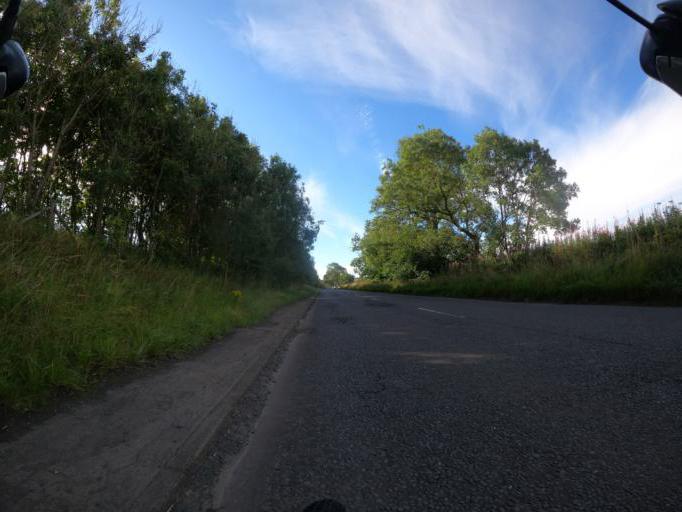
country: GB
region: Scotland
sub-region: Edinburgh
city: Newbridge
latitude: 55.9218
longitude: -3.4121
